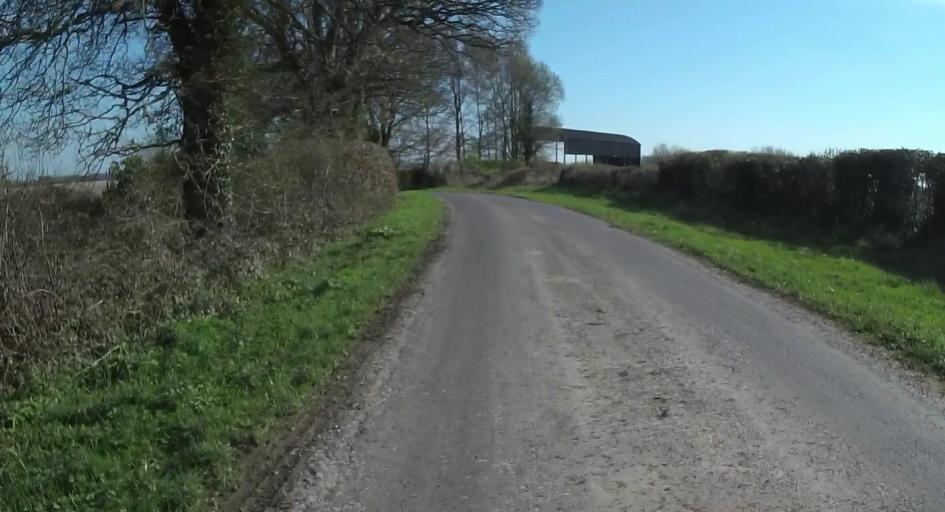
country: GB
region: England
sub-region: Hampshire
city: Highclere
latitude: 51.2625
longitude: -1.3875
